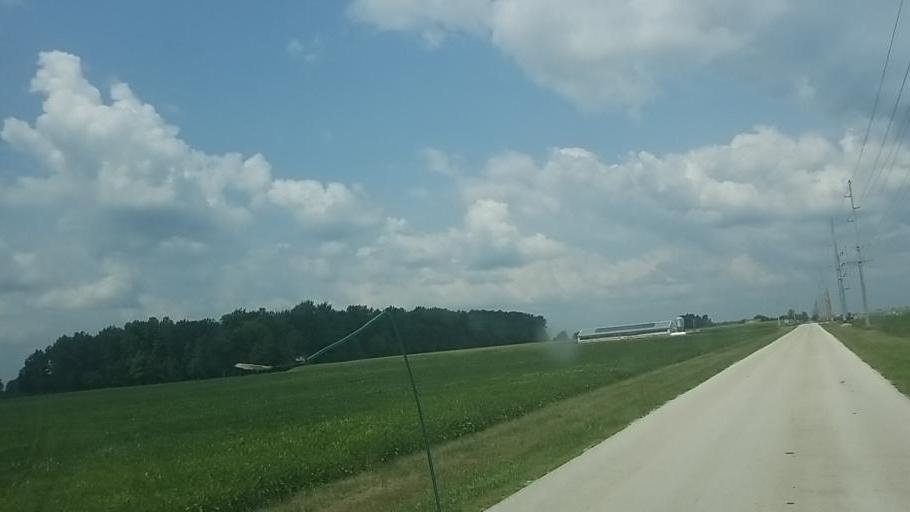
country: US
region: Ohio
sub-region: Wyandot County
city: Carey
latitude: 40.9648
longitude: -83.3048
